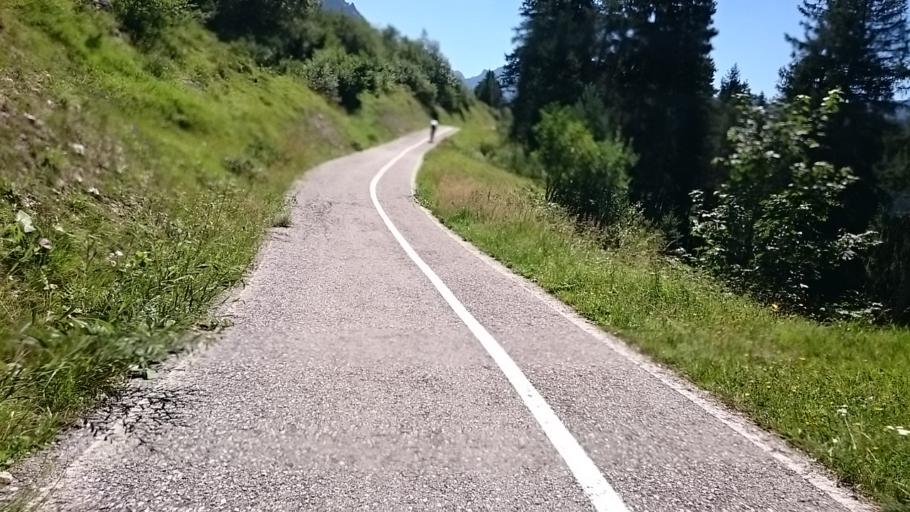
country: IT
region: Veneto
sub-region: Provincia di Belluno
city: San Vito
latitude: 46.4836
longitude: 12.1928
